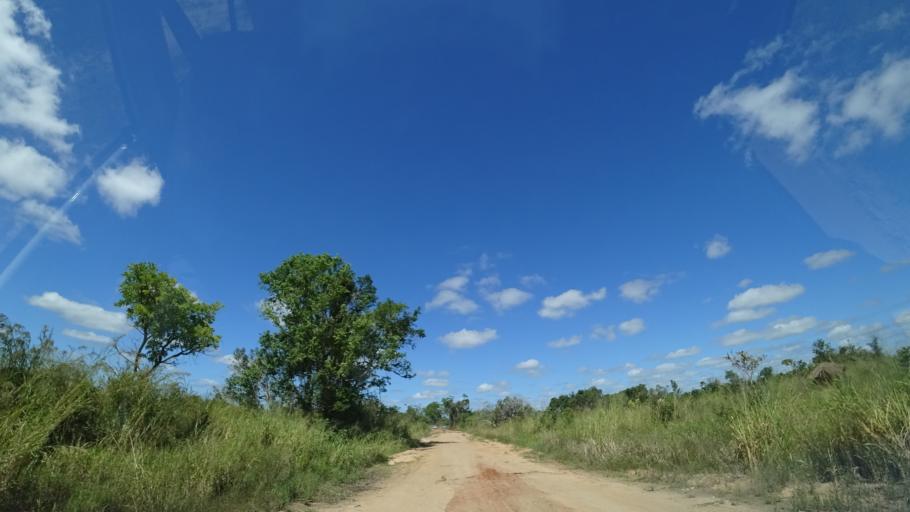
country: MZ
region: Sofala
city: Dondo
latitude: -19.2808
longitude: 34.6839
